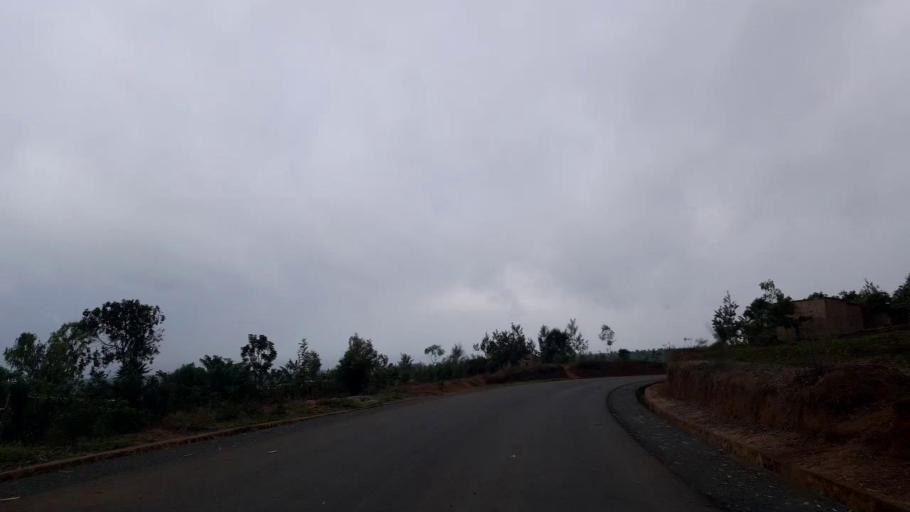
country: RW
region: Northern Province
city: Byumba
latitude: -1.4238
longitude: 30.2694
